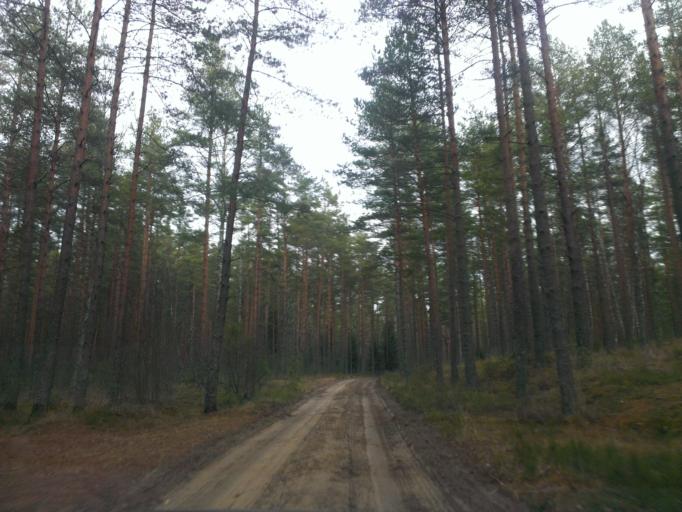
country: LV
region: Riga
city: Bergi
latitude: 56.9986
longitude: 24.3414
